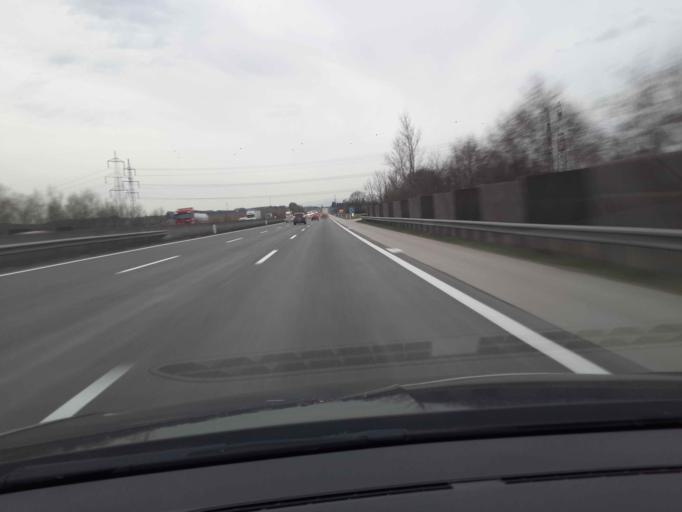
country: AT
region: Lower Austria
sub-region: Politischer Bezirk Amstetten
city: Strengberg
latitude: 48.1188
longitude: 14.6213
